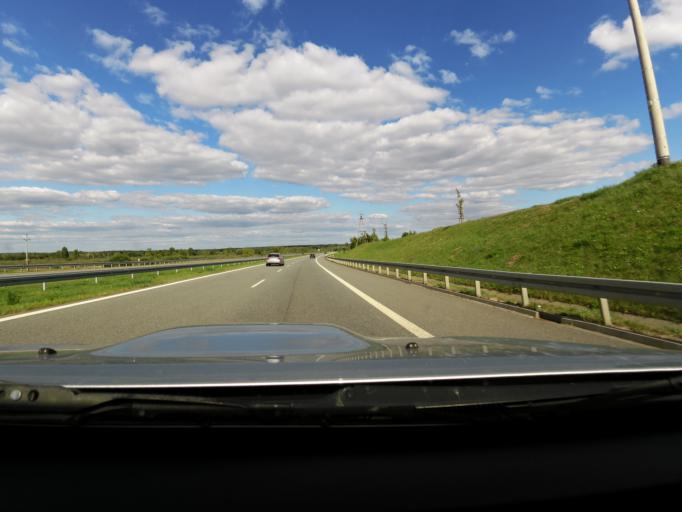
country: PL
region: Warmian-Masurian Voivodeship
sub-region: Powiat elcki
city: Elk
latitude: 53.8443
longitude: 22.3569
